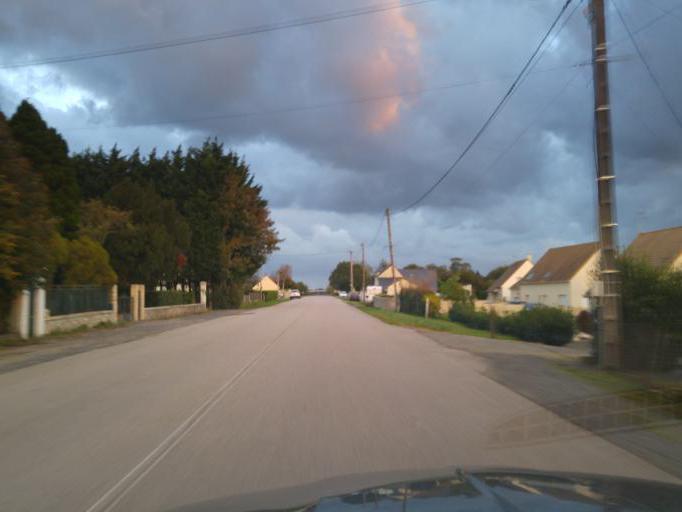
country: FR
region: Lower Normandy
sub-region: Departement du Calvados
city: Grandcamp-Maisy
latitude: 49.3421
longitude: -0.9975
